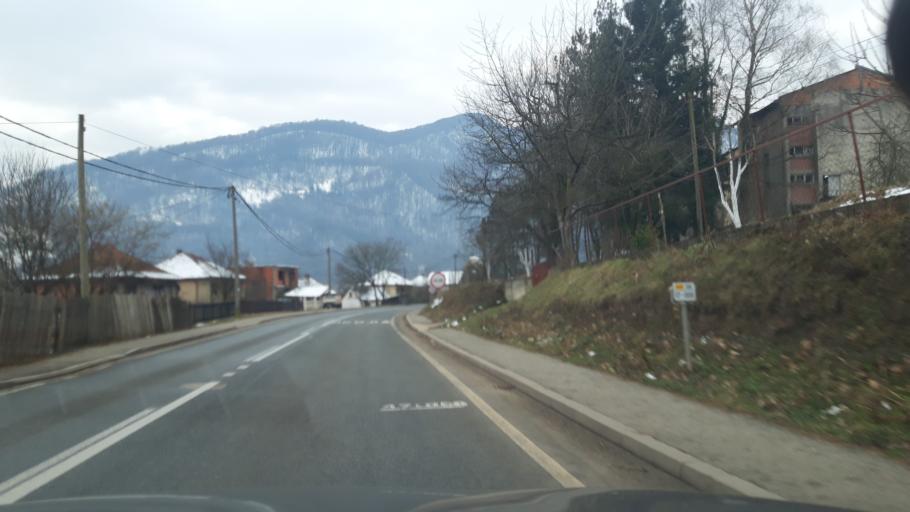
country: RS
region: Central Serbia
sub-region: Macvanski Okrug
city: Mali Zvornik
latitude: 44.2888
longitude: 19.1491
